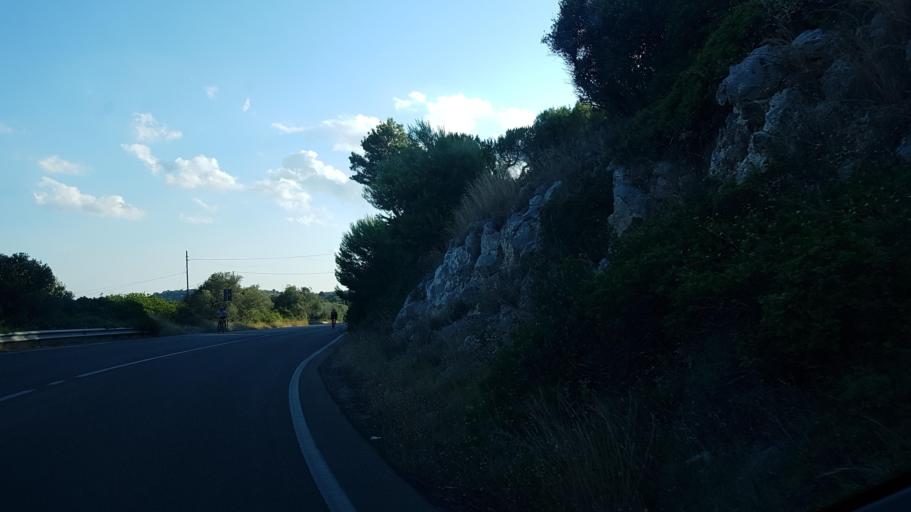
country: IT
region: Apulia
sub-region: Provincia di Lecce
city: Castro
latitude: 40.0004
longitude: 18.4215
